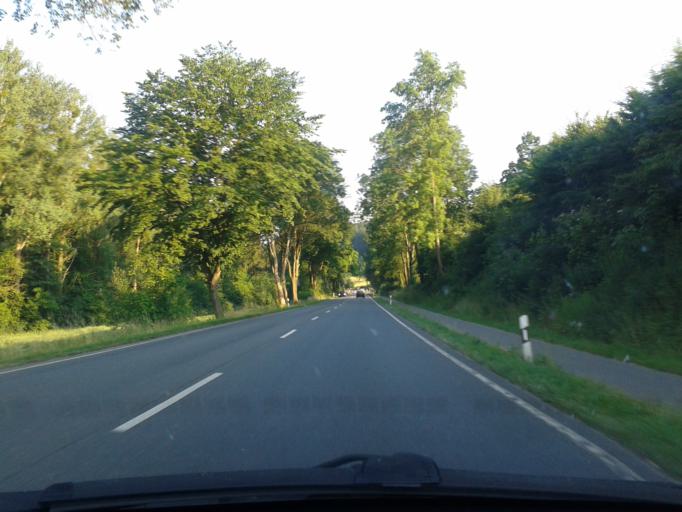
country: DE
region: North Rhine-Westphalia
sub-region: Regierungsbezirk Detmold
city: Horn
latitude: 51.9058
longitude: 8.9269
